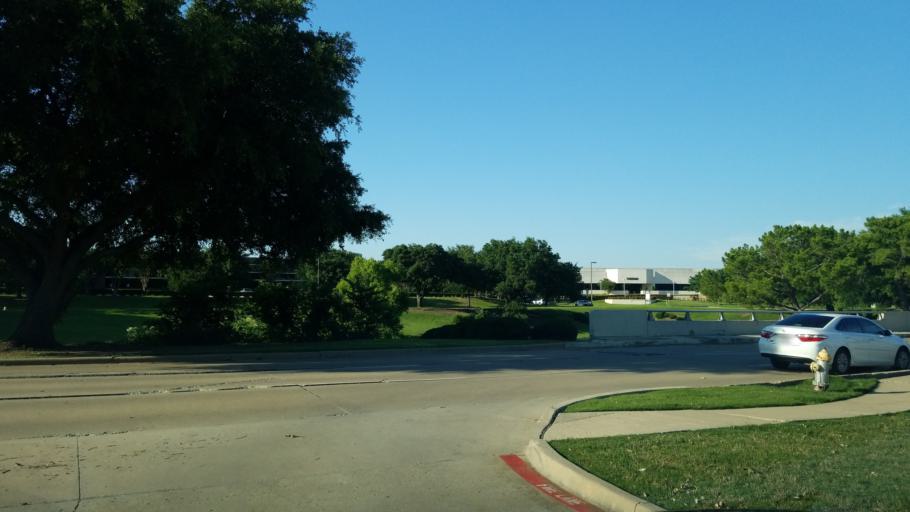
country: US
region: Texas
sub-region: Dallas County
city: Coppell
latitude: 32.9103
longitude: -96.9888
